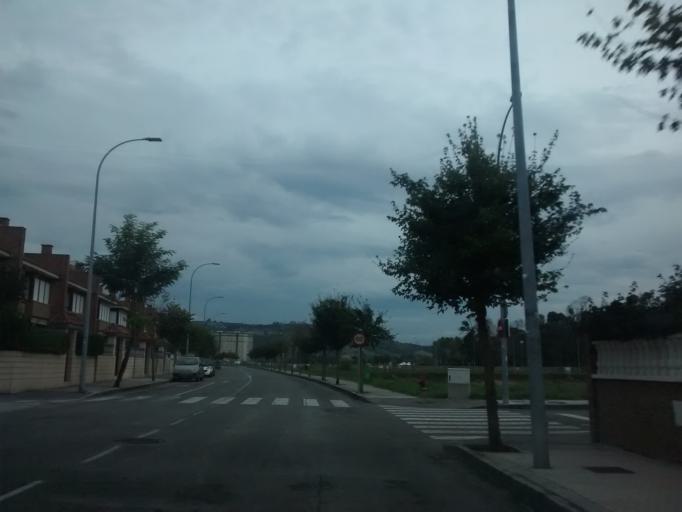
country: ES
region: Cantabria
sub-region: Provincia de Cantabria
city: Colindres
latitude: 43.4203
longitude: -3.4472
